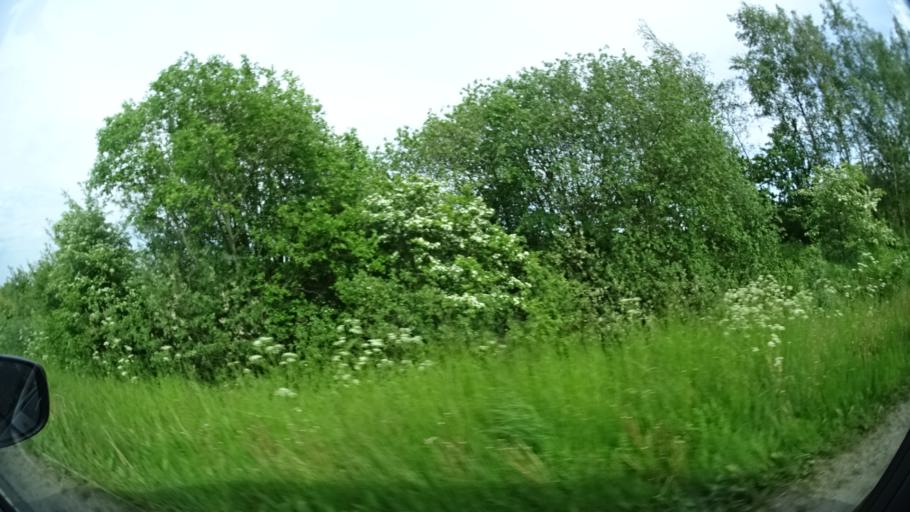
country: DK
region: Central Jutland
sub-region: Arhus Kommune
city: Malling
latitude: 56.0481
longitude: 10.1903
